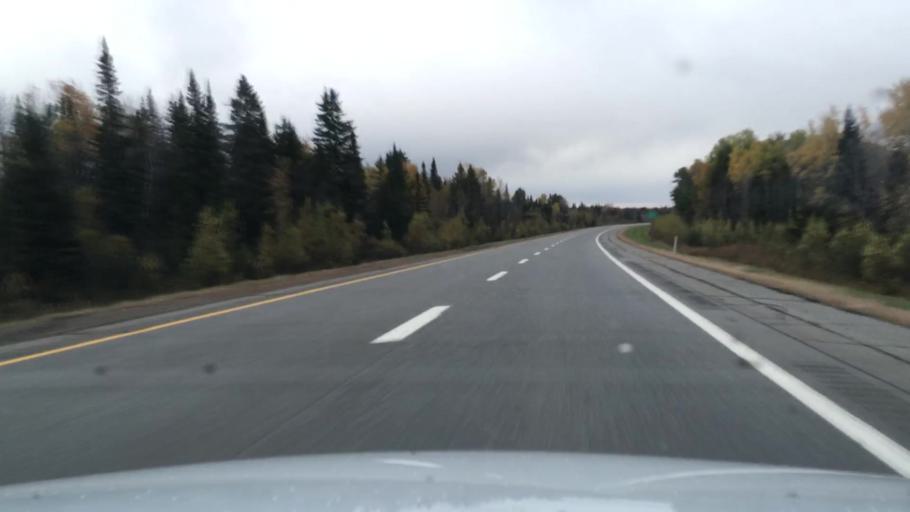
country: US
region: Maine
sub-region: Penobscot County
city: Greenbush
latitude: 45.1214
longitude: -68.6952
